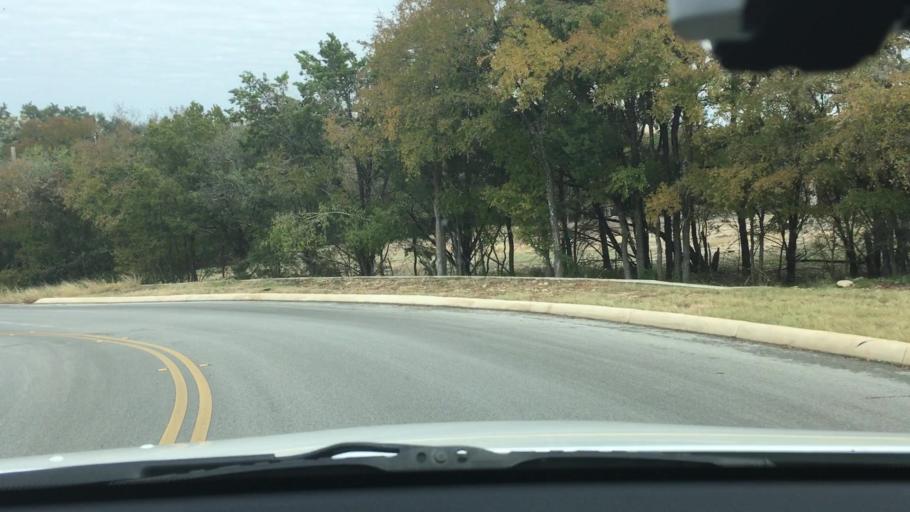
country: US
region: Texas
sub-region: Bexar County
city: Hollywood Park
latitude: 29.5984
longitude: -98.4152
